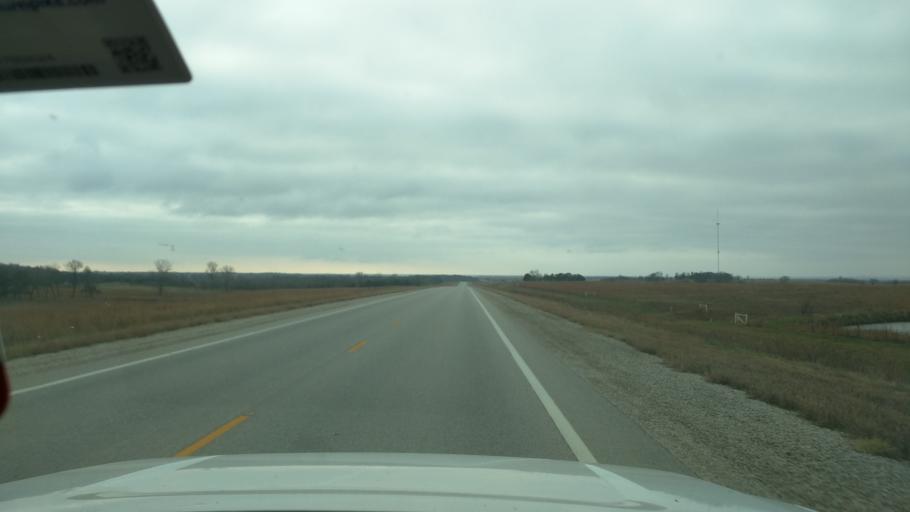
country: US
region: Kansas
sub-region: Elk County
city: Howard
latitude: 37.5573
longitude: -96.2532
